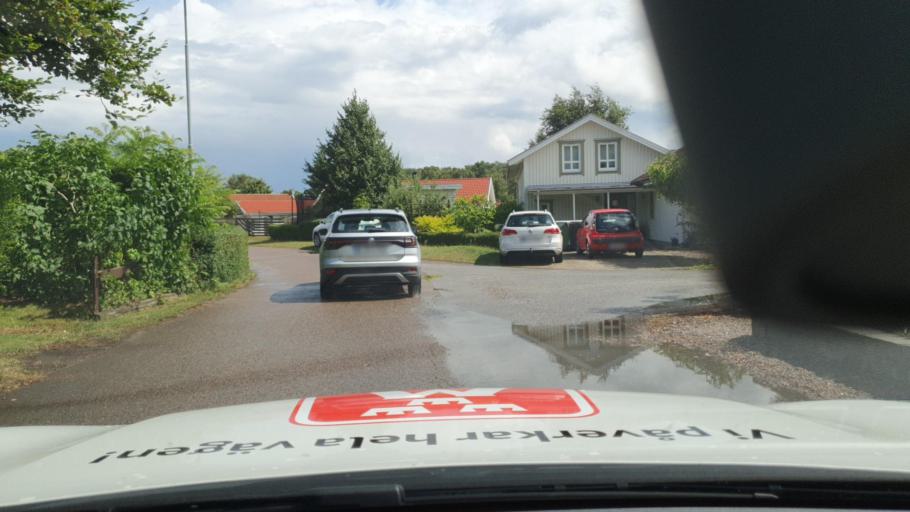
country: SE
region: Skane
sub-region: Angelholms Kommun
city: Vejbystrand
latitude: 56.2318
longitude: 12.6790
